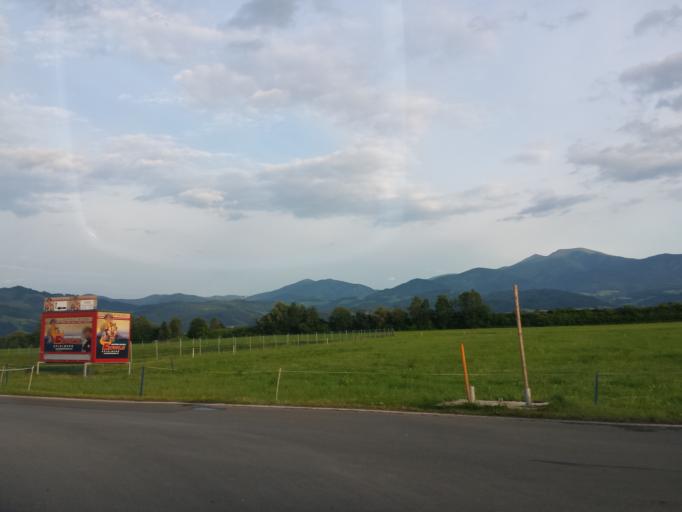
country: AT
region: Styria
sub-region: Politischer Bezirk Murtal
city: Flatschach
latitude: 47.2157
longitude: 14.7663
